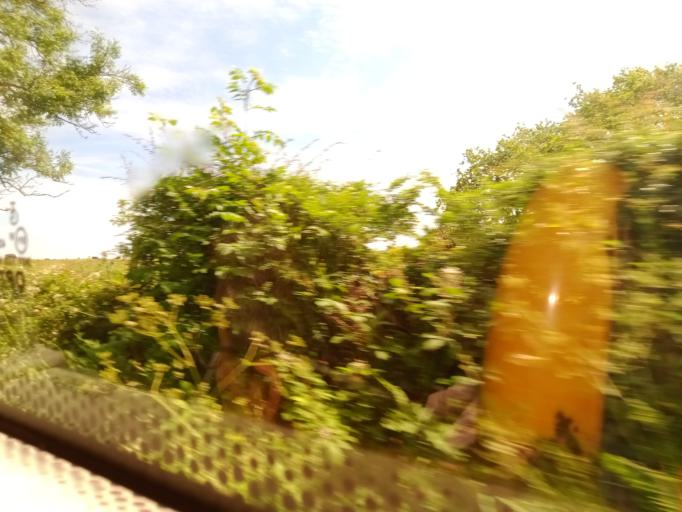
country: GB
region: Wales
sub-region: Anglesey
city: Beaumaris
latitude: 53.2582
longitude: -4.1206
